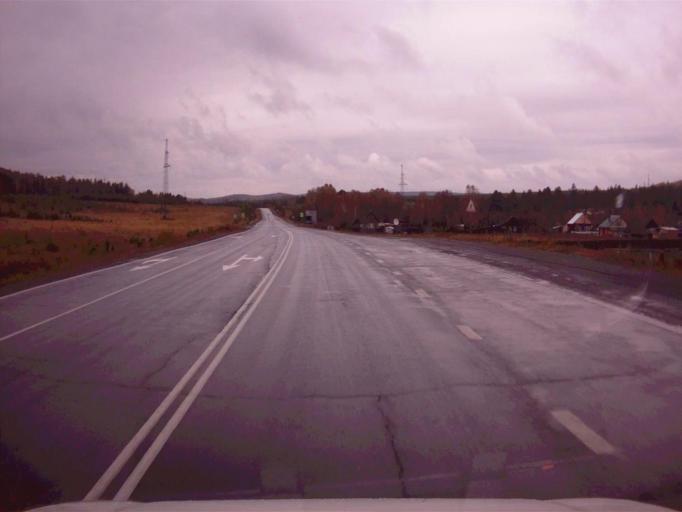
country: RU
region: Chelyabinsk
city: Verkhniy Ufaley
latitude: 56.0040
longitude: 60.3281
